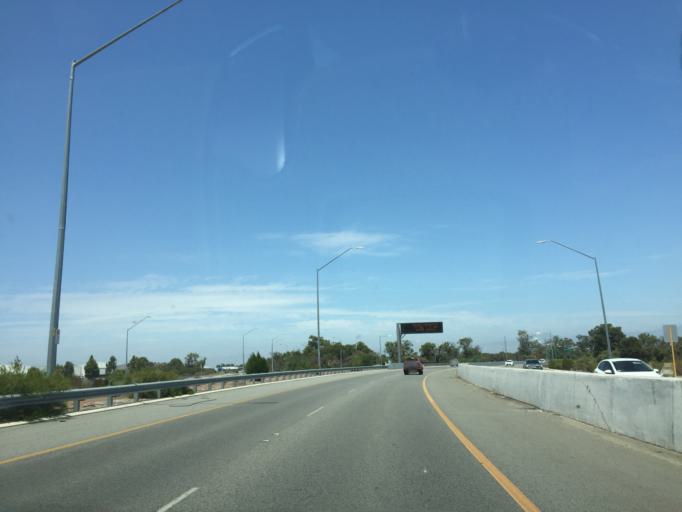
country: AU
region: Western Australia
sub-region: Belmont
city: Kewdale
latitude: -31.9622
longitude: 115.9661
